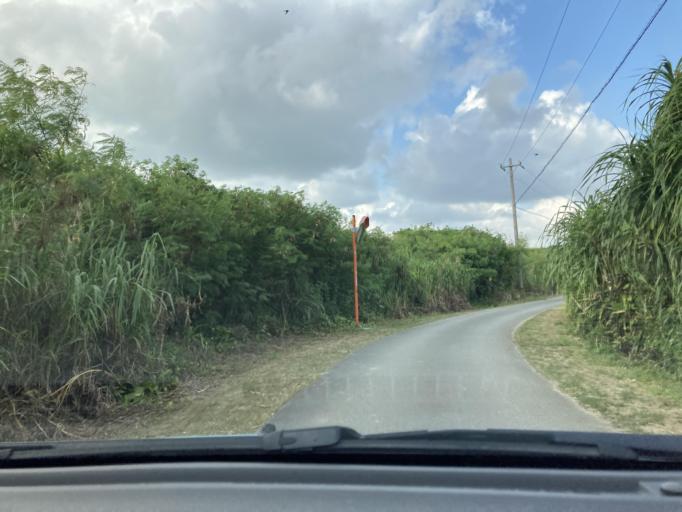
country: JP
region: Okinawa
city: Itoman
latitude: 26.0805
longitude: 127.6688
